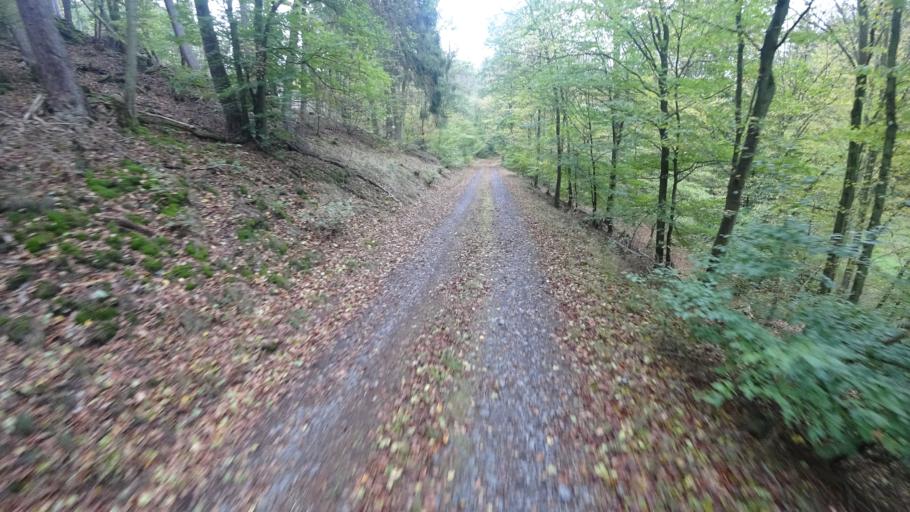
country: DE
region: Rheinland-Pfalz
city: Isselbach
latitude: 50.4087
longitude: 7.9114
